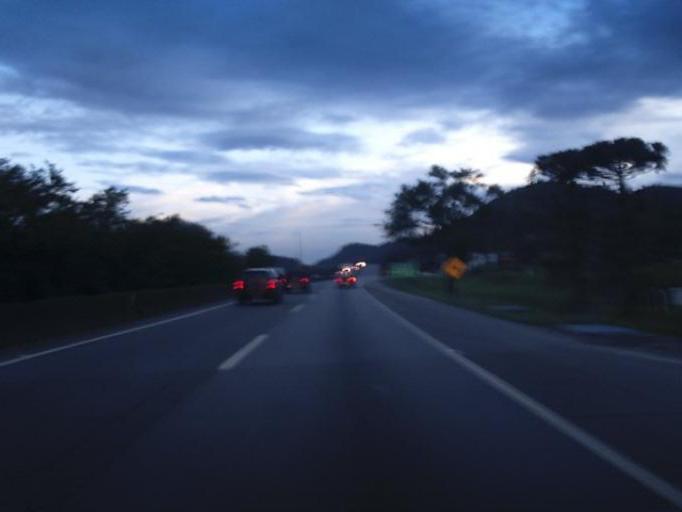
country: BR
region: Santa Catarina
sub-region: Joinville
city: Joinville
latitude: -26.1989
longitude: -48.9127
